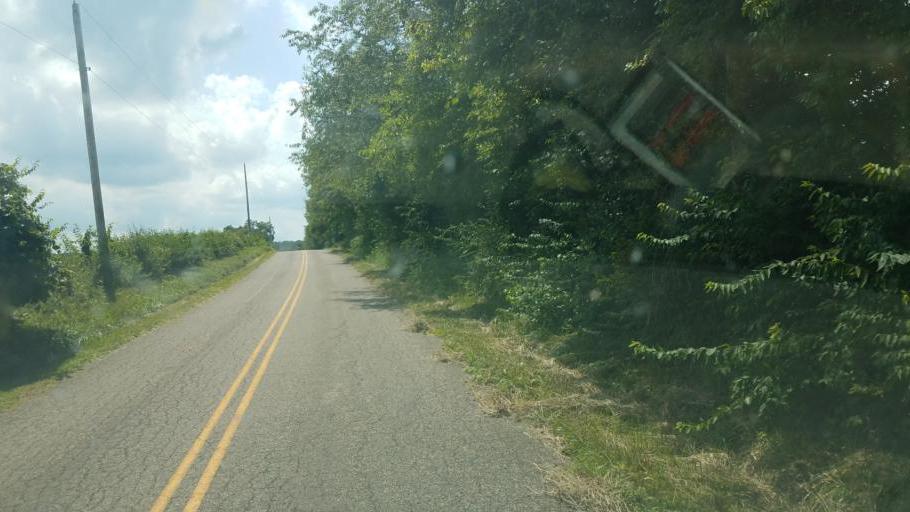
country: US
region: Ohio
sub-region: Knox County
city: Mount Vernon
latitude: 40.3929
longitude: -82.5793
